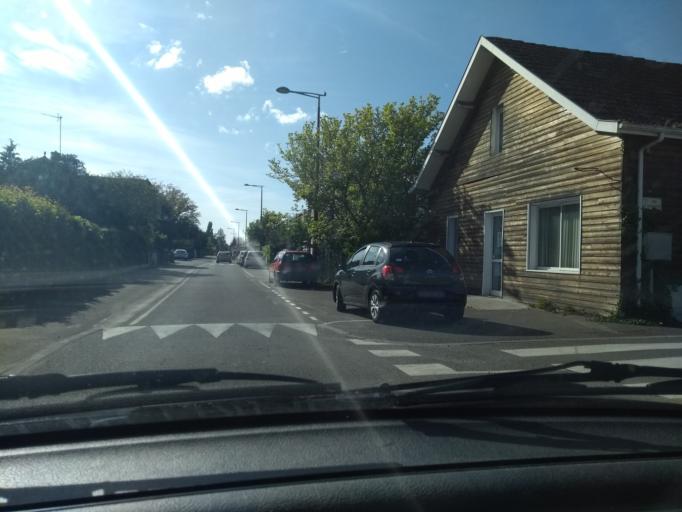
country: FR
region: Aquitaine
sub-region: Departement des Landes
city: Parentis-en-Born
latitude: 44.3487
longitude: -1.0761
